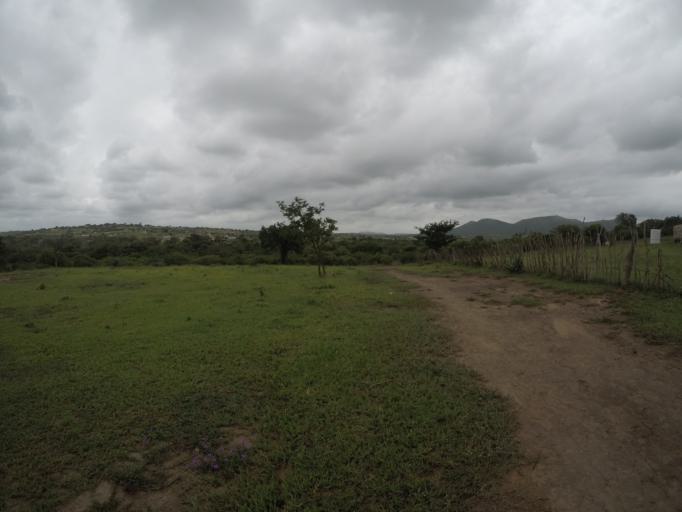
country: ZA
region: KwaZulu-Natal
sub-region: uThungulu District Municipality
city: Empangeni
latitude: -28.5910
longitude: 31.8441
